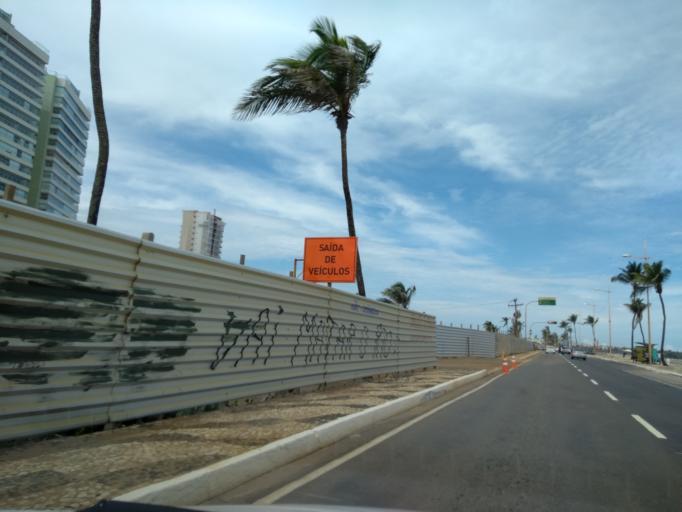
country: BR
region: Bahia
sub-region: Lauro De Freitas
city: Lauro de Freitas
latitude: -12.9594
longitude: -38.3937
